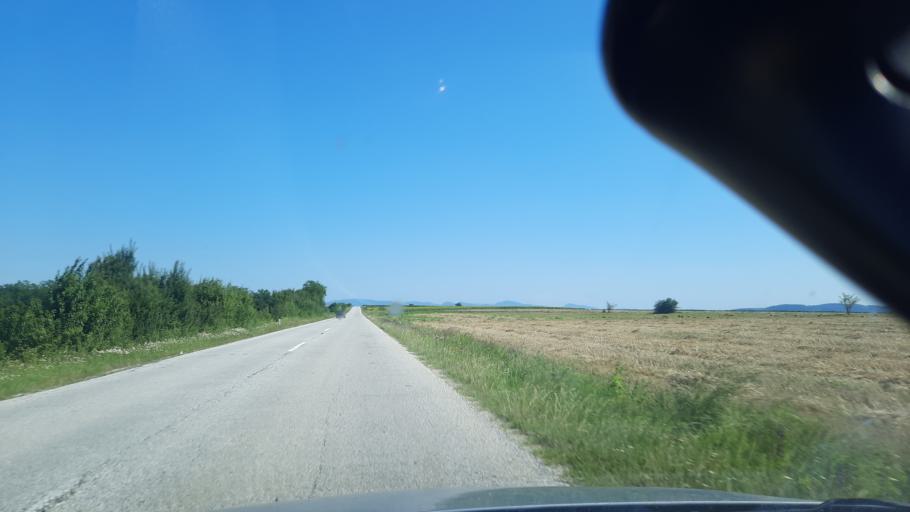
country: RS
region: Central Serbia
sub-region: Branicevski Okrug
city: Malo Crnice
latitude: 44.5692
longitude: 21.4282
